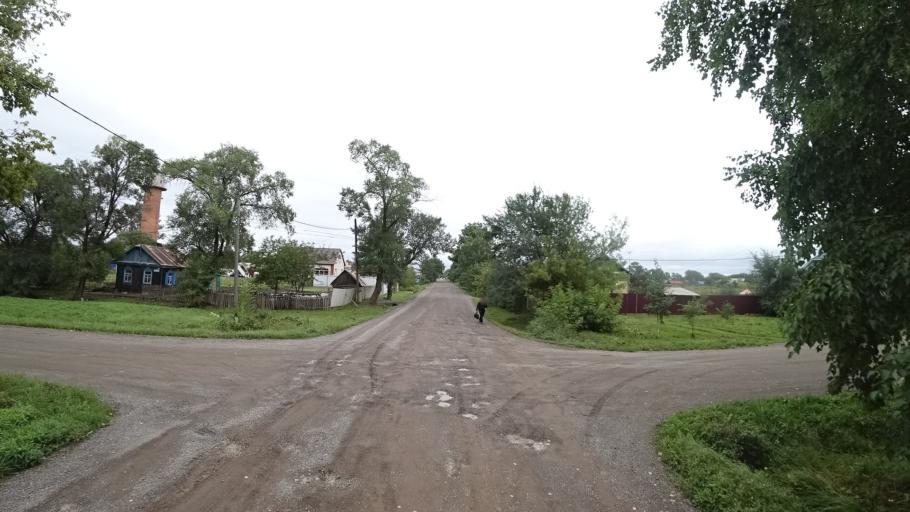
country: RU
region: Primorskiy
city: Chernigovka
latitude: 44.3369
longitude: 132.5721
